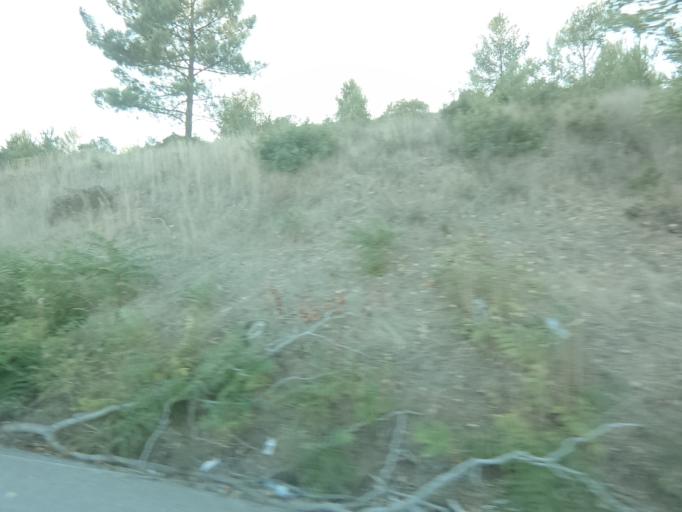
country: PT
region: Setubal
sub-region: Palmela
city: Quinta do Anjo
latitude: 38.5264
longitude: -8.9824
